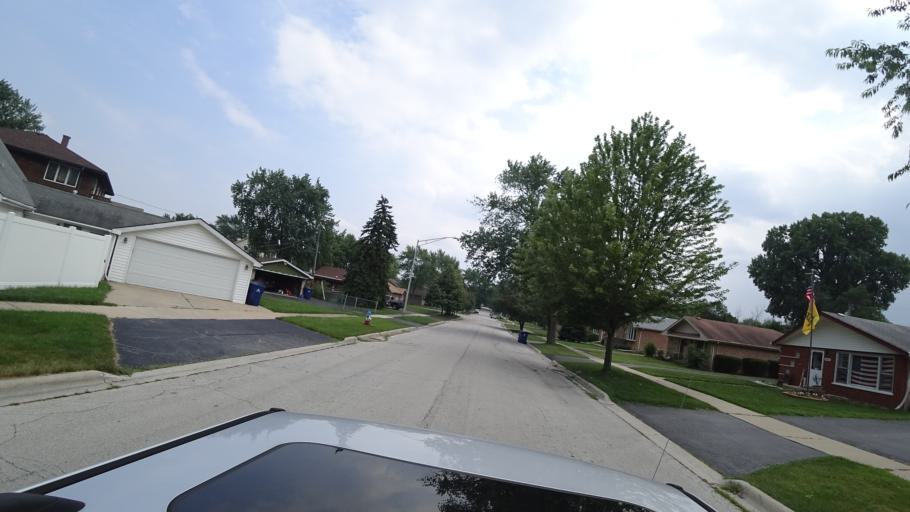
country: US
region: Illinois
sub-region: Cook County
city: Chicago Ridge
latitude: 41.7009
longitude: -87.7756
